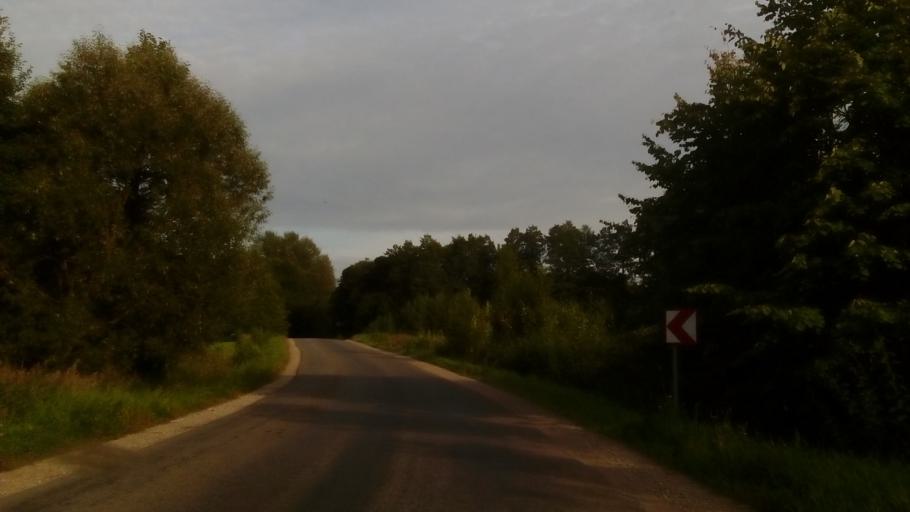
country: LT
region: Alytaus apskritis
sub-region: Alytus
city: Alytus
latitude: 54.3279
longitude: 23.9198
